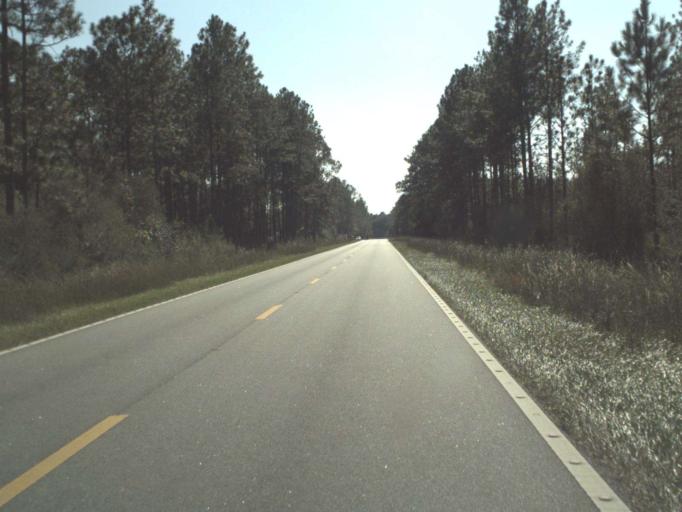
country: US
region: Florida
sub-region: Gulf County
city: Wewahitchka
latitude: 30.0375
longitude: -84.9836
